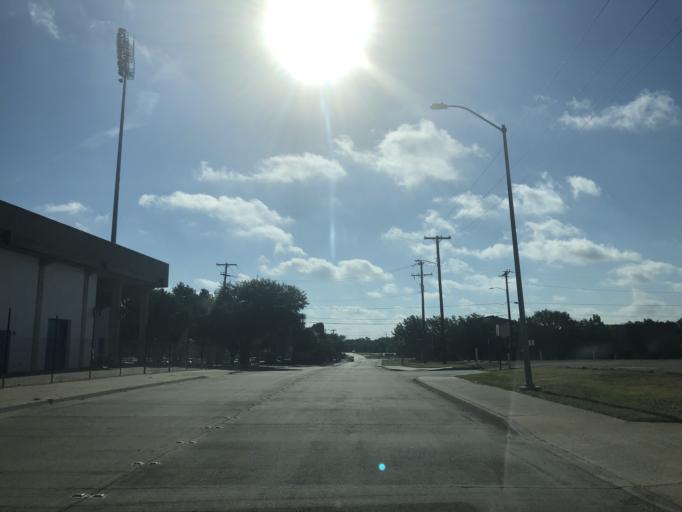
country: US
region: Texas
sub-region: Dallas County
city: Duncanville
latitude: 32.6586
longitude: -96.9284
